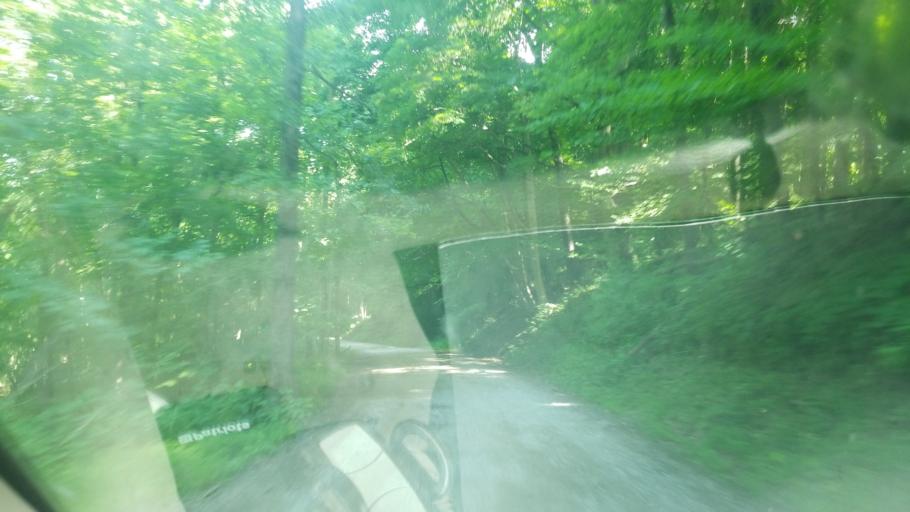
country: US
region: Ohio
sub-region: Holmes County
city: Millersburg
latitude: 40.4696
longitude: -81.9634
